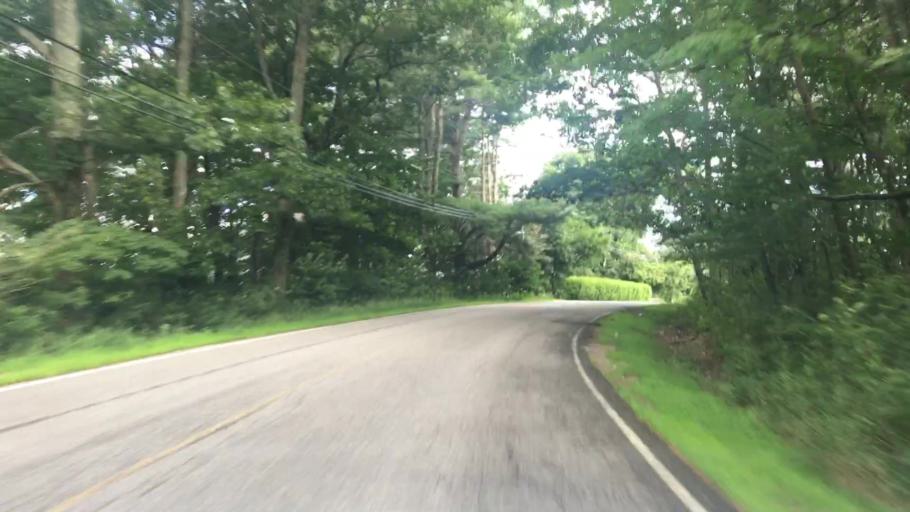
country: US
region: Maine
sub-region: York County
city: West Kennebunk
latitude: 43.4559
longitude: -70.6176
